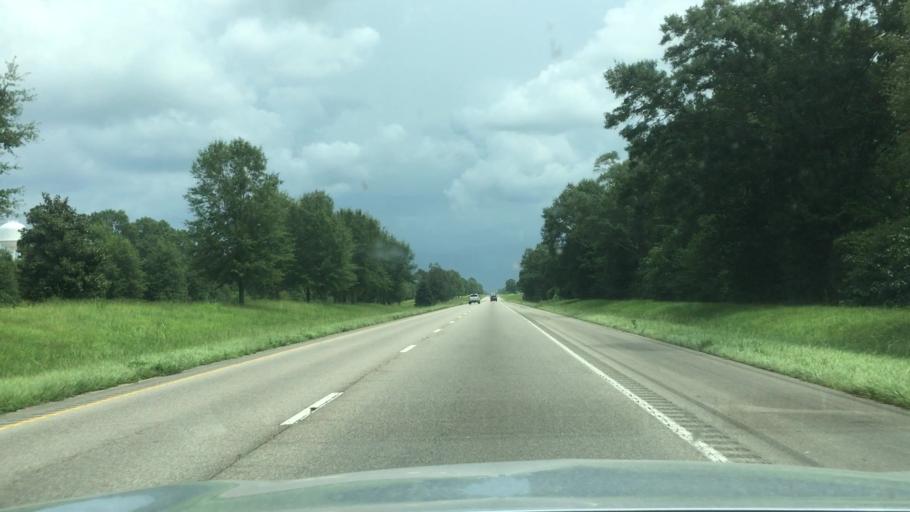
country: US
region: Mississippi
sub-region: Pearl River County
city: Carriere
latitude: 30.5733
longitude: -89.6329
